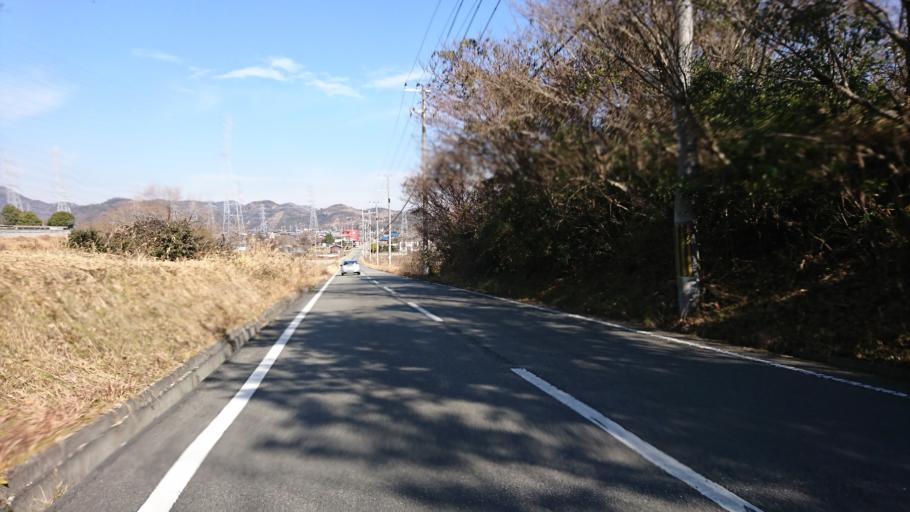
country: JP
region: Hyogo
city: Kakogawacho-honmachi
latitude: 34.8009
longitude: 134.8583
